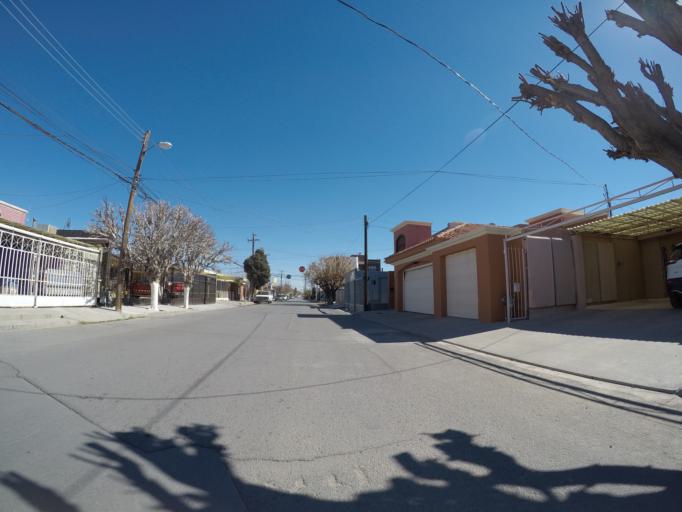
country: MX
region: Chihuahua
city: Ciudad Juarez
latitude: 31.7323
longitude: -106.4433
